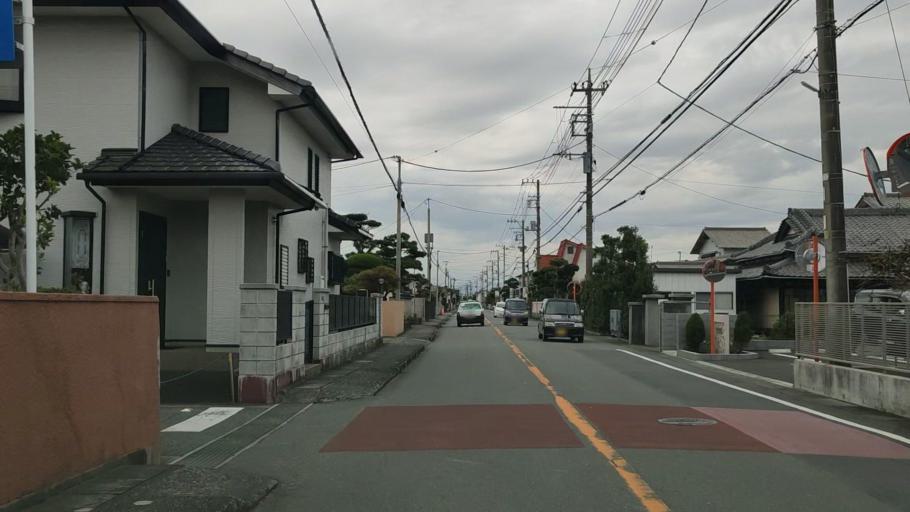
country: JP
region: Shizuoka
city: Numazu
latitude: 35.1121
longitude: 138.8286
